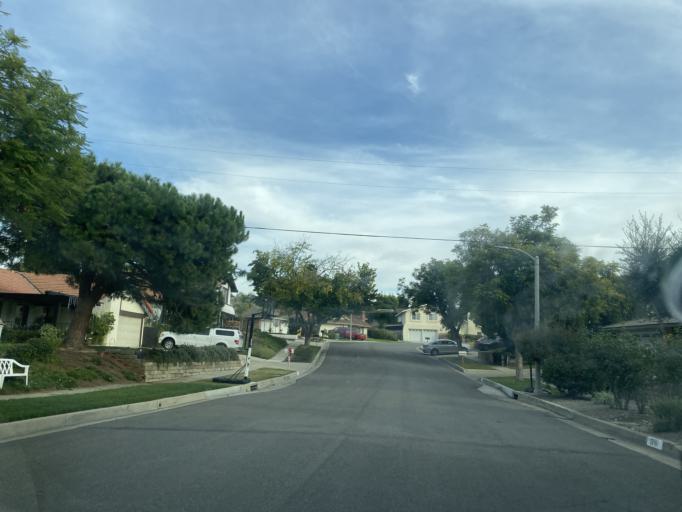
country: US
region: California
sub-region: Orange County
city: Brea
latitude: 33.9026
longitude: -117.8958
